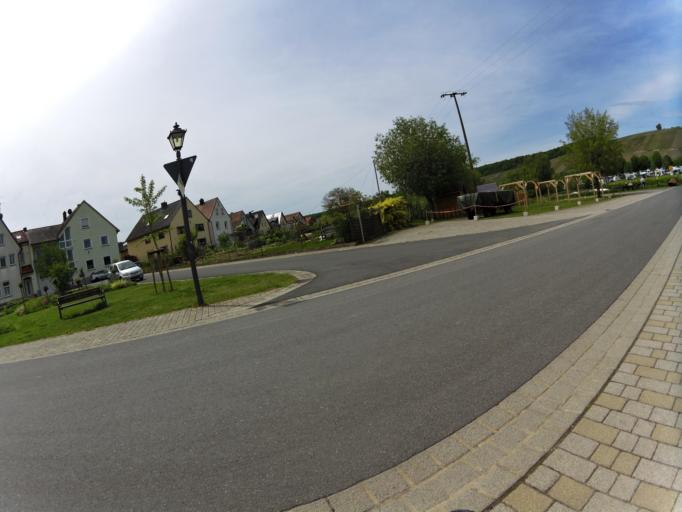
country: DE
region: Bavaria
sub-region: Regierungsbezirk Unterfranken
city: Nordheim
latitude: 49.8596
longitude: 10.1798
